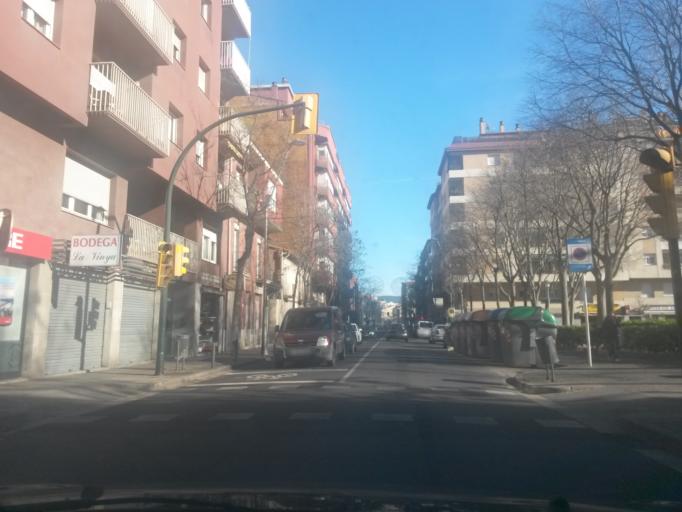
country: ES
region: Catalonia
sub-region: Provincia de Girona
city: Salt
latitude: 41.9767
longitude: 2.8025
